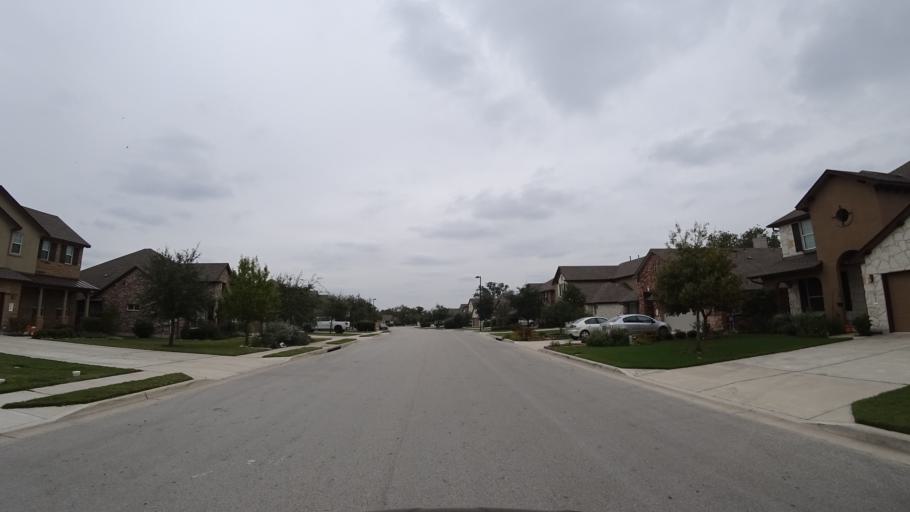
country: US
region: Texas
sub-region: Travis County
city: Shady Hollow
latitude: 30.1797
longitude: -97.9056
